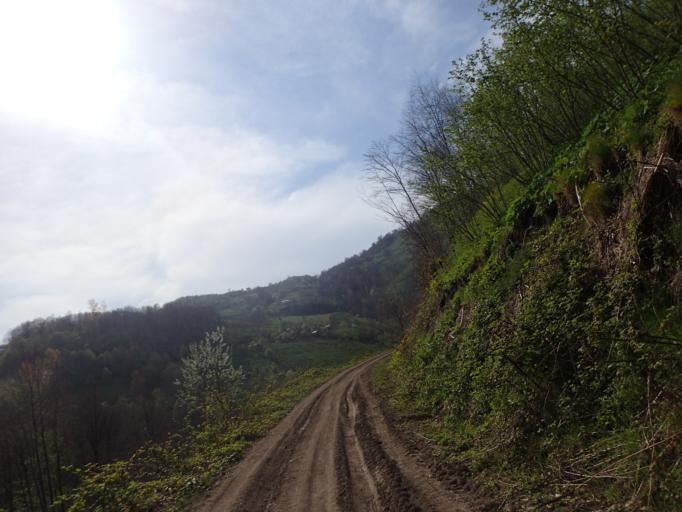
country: TR
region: Ordu
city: Aybasti
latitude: 40.7207
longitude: 37.2990
